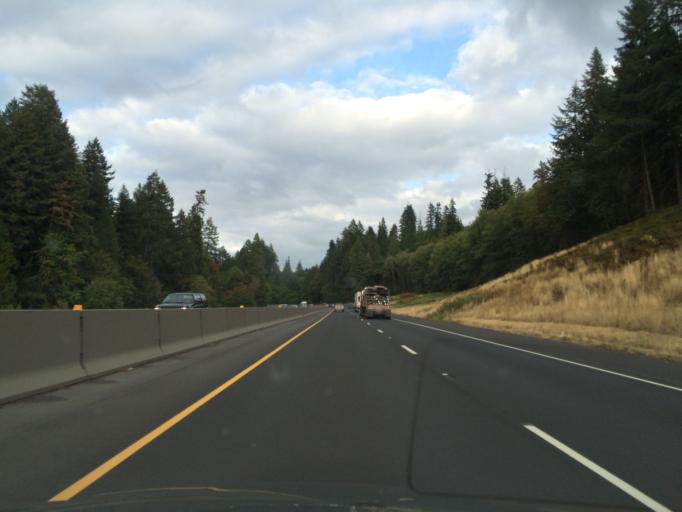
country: US
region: Oregon
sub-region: Lane County
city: Cottage Grove
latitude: 43.7506
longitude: -123.1709
